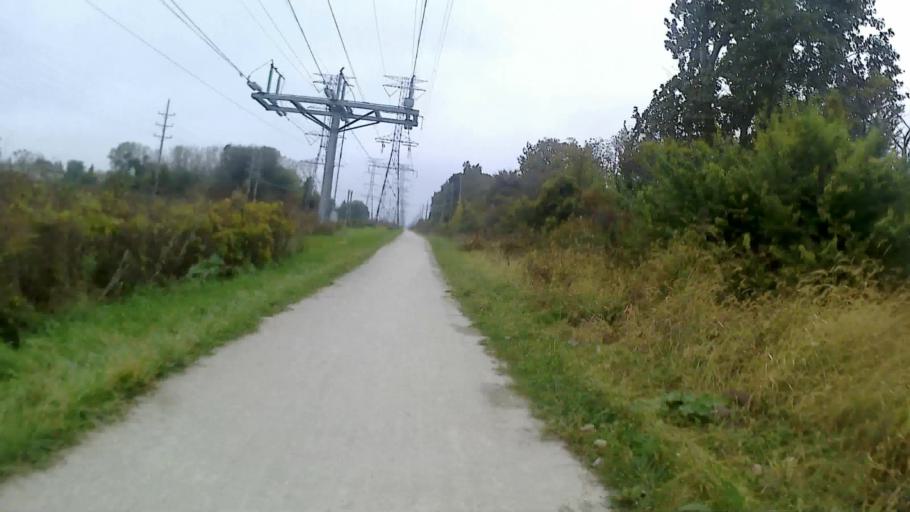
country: US
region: Illinois
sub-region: DuPage County
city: Warrenville
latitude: 41.7944
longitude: -88.2459
